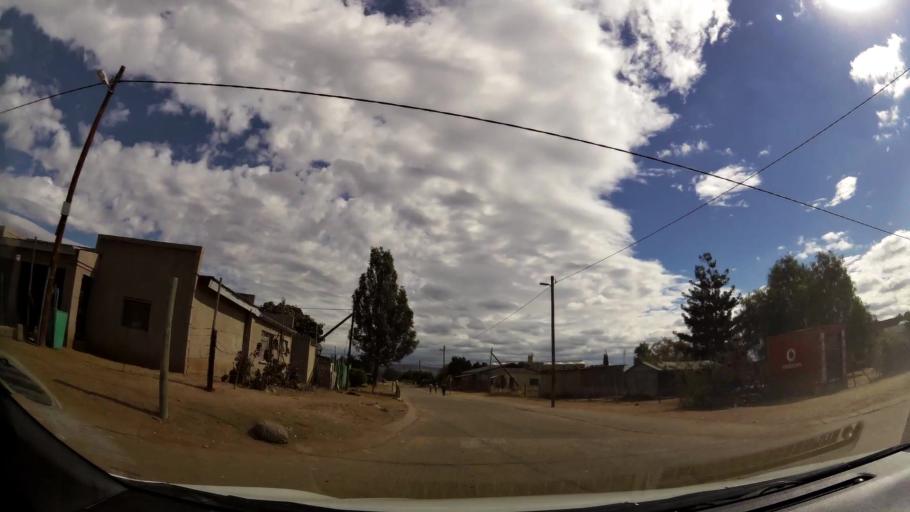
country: ZA
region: Limpopo
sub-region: Waterberg District Municipality
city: Bela-Bela
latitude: -24.8890
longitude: 28.3084
